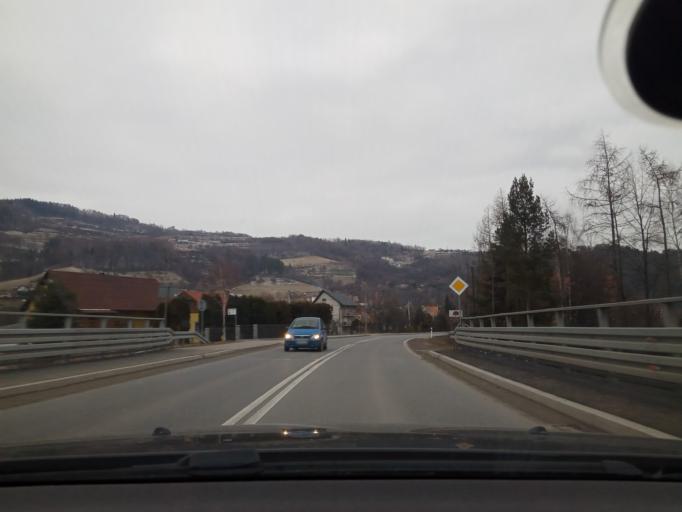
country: PL
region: Lesser Poland Voivodeship
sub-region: Powiat nowosadecki
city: Lacko
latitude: 49.5417
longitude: 20.4042
